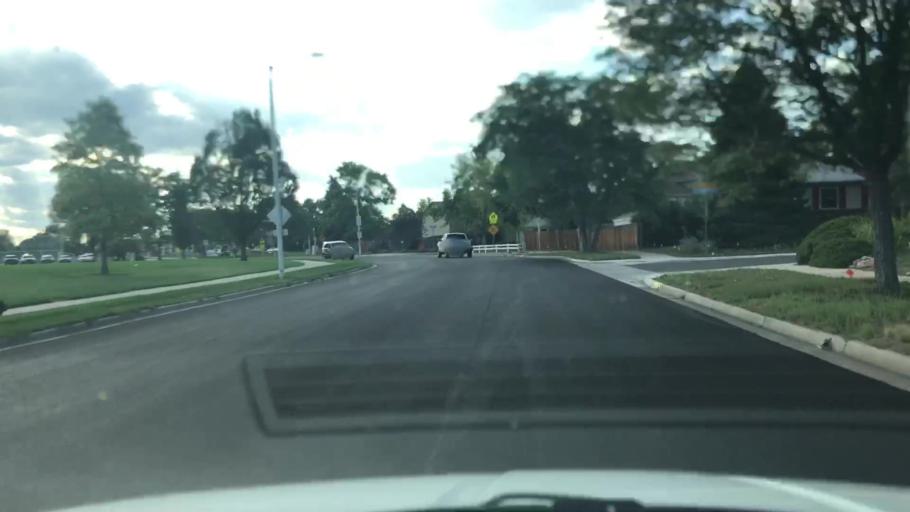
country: US
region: Colorado
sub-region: Broomfield County
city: Broomfield
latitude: 39.9223
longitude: -105.0371
